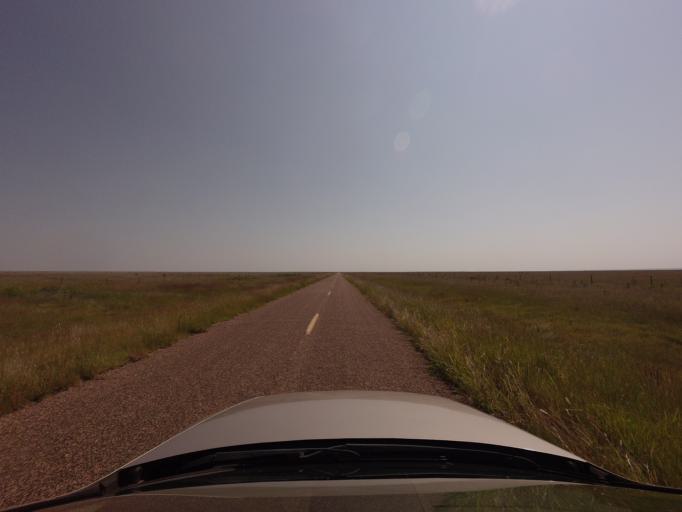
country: US
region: New Mexico
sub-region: Curry County
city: Cannon Air Force Base
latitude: 34.6332
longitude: -103.4345
